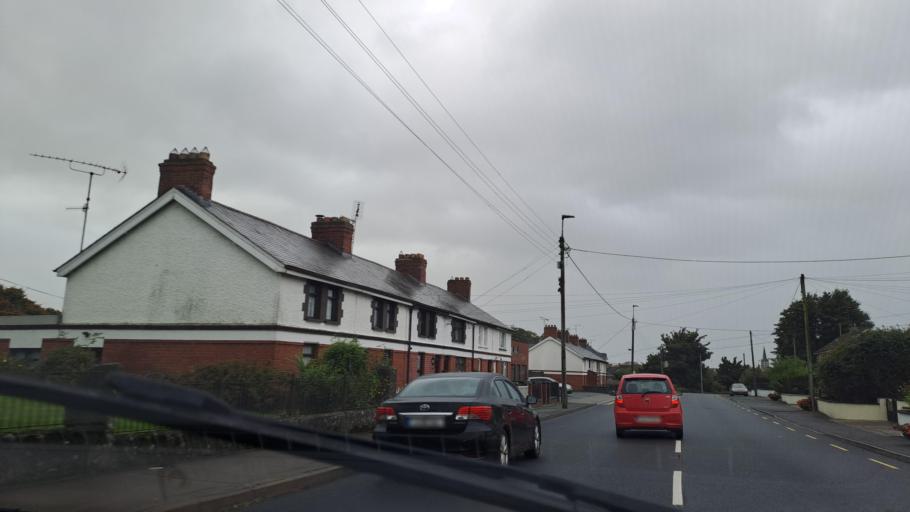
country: IE
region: Ulster
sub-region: County Monaghan
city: Carrickmacross
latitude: 53.9797
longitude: -6.7173
